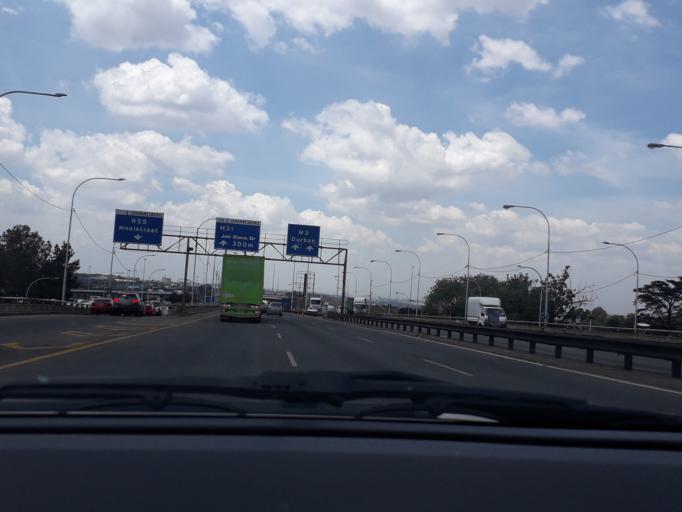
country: ZA
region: Gauteng
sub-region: City of Johannesburg Metropolitan Municipality
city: Johannesburg
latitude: -26.2129
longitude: 28.0500
